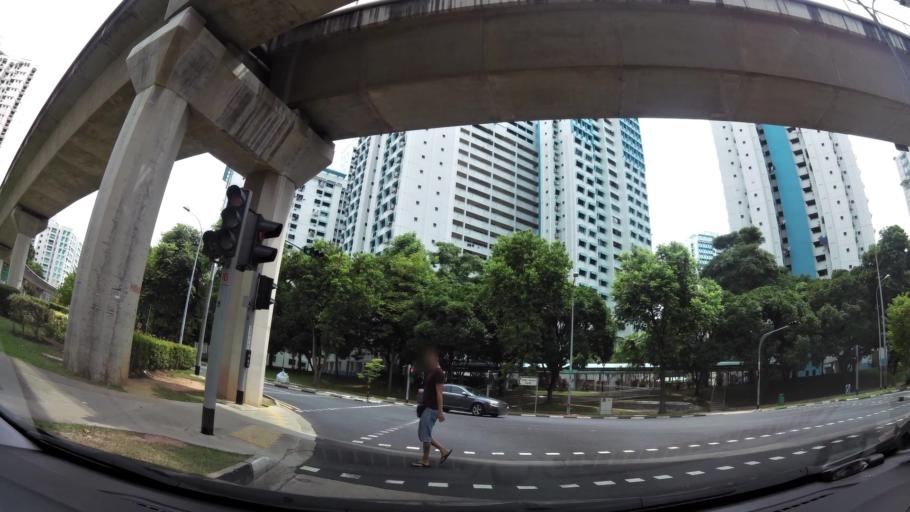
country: MY
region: Johor
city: Johor Bahru
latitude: 1.3784
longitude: 103.7646
